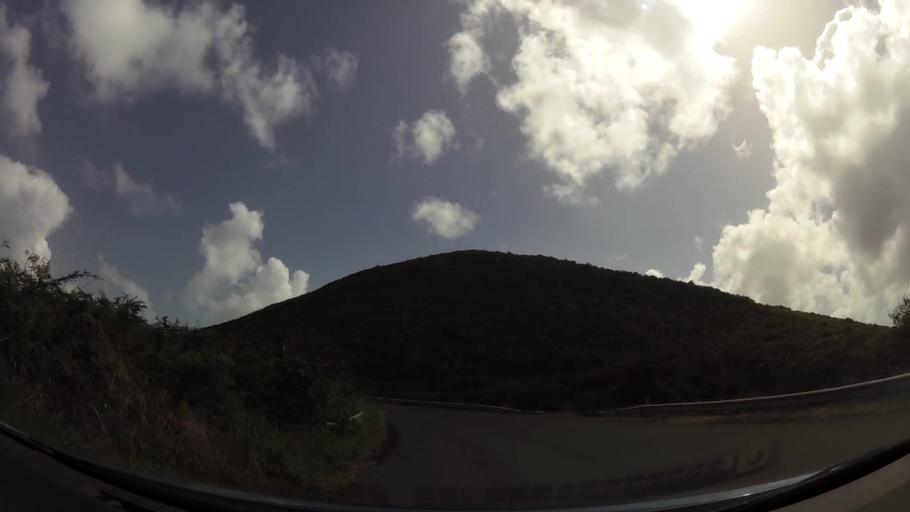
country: KN
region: Saint George Basseterre
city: Basseterre
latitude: 17.2828
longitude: -62.6847
